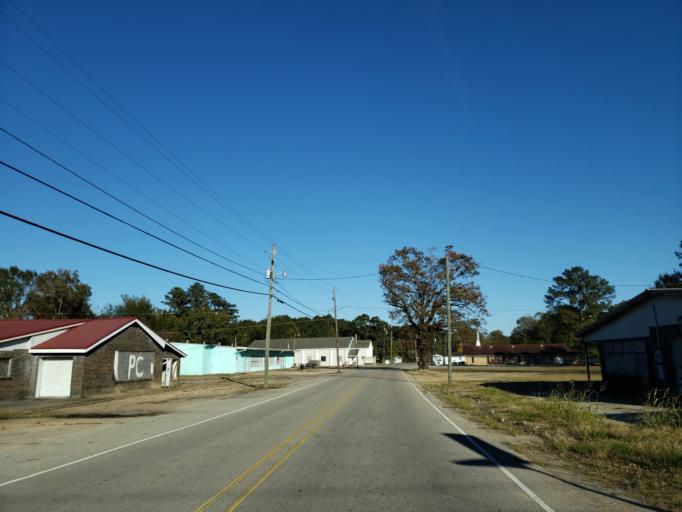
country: US
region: Mississippi
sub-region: Forrest County
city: Hattiesburg
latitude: 31.2778
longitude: -89.2655
